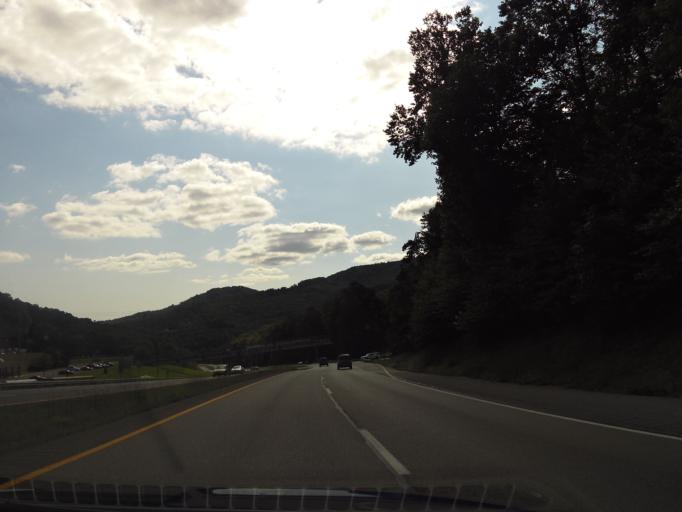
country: US
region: Kentucky
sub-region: Bell County
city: Pineville
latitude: 36.7146
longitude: -83.6911
